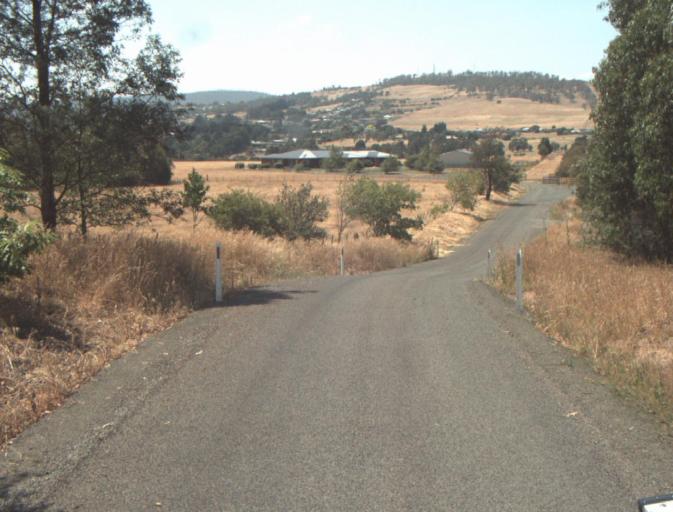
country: AU
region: Tasmania
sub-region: Launceston
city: Newstead
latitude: -41.4704
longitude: 147.1909
